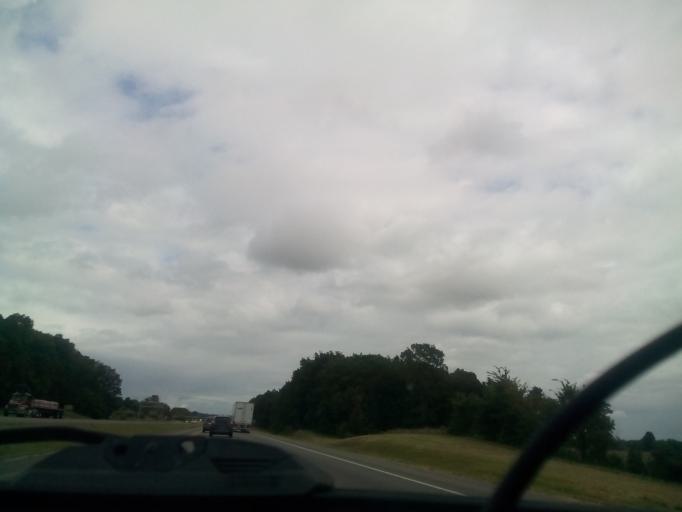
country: US
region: Ohio
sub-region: Williams County
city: Montpelier
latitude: 41.6283
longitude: -84.7369
